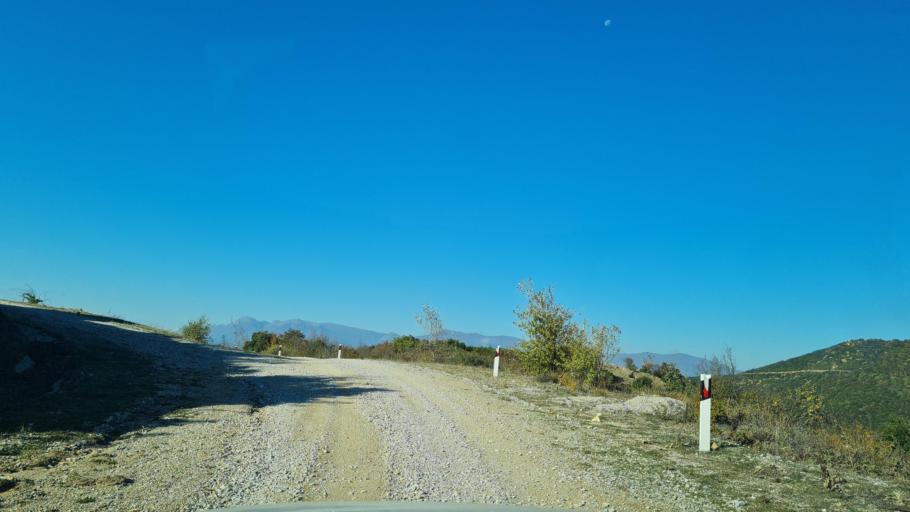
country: MK
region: Bogdanci
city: Bogdanci
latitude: 41.2225
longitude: 22.5494
